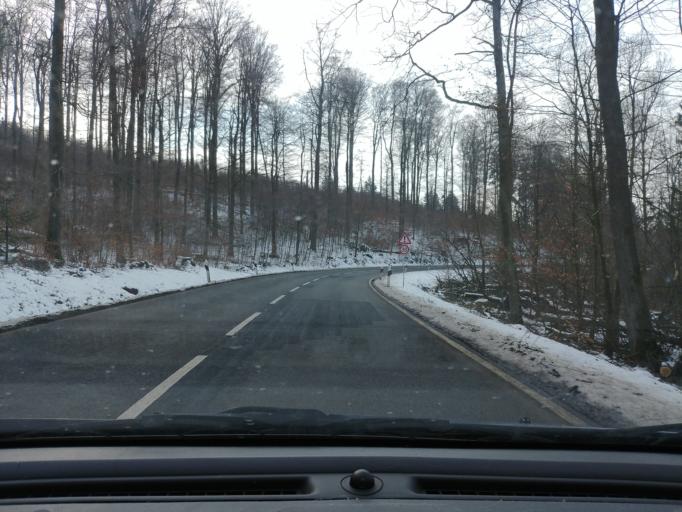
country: DE
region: Lower Saxony
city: Derental
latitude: 51.6807
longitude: 9.4476
